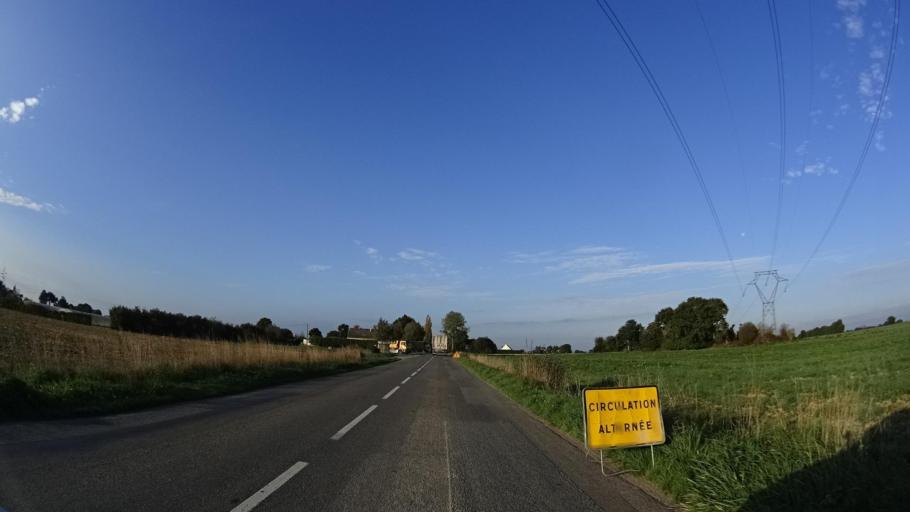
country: FR
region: Brittany
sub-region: Departement d'Ille-et-Vilaine
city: Quedillac
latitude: 48.2561
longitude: -2.1162
